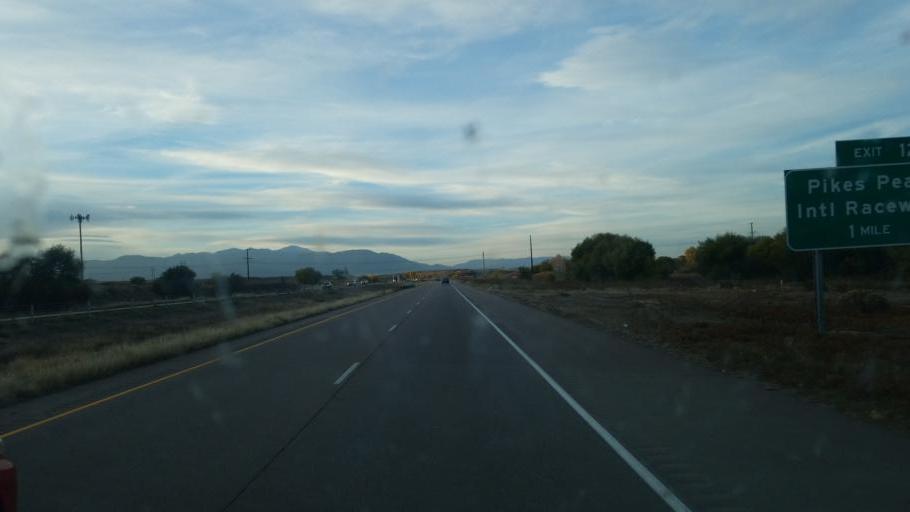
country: US
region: Colorado
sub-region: El Paso County
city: Fountain
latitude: 38.5761
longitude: -104.6606
